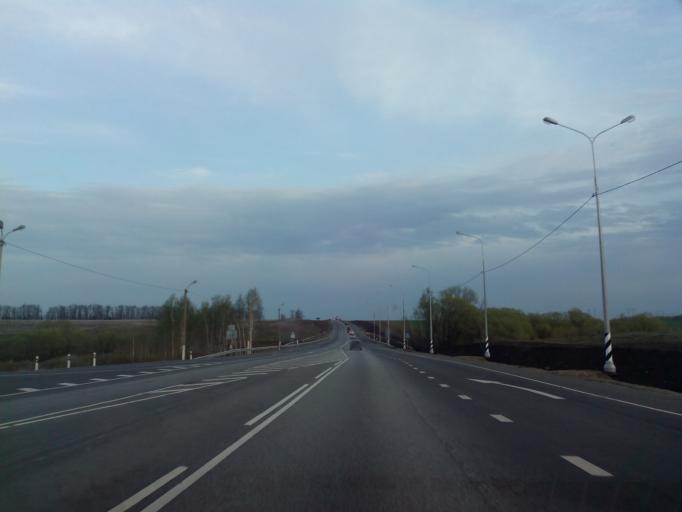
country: RU
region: Rjazan
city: Ryazhsk
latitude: 53.5565
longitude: 40.0535
